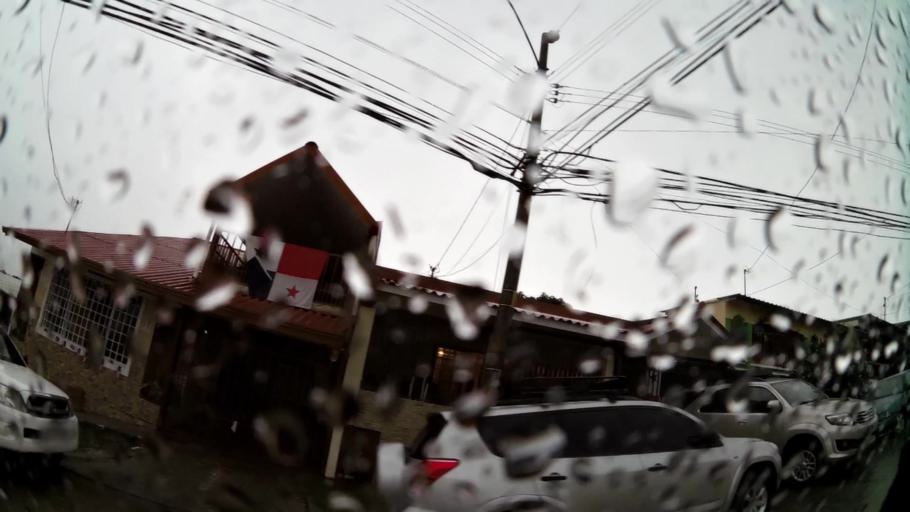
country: PA
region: Panama
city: San Miguelito
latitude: 9.0537
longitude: -79.4738
